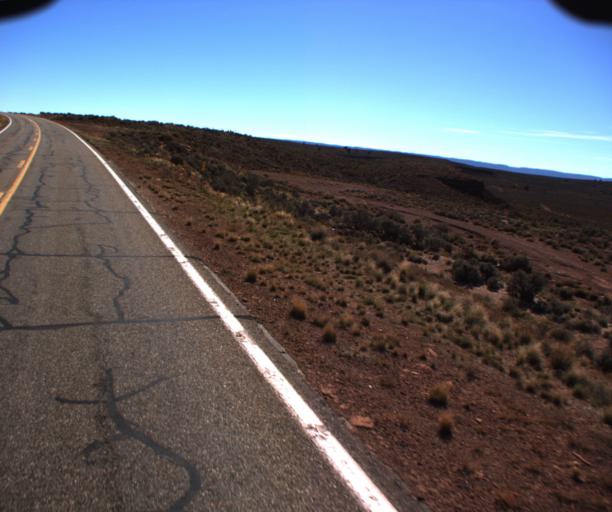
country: US
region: Arizona
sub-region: Coconino County
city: Fredonia
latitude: 36.9088
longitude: -112.4131
